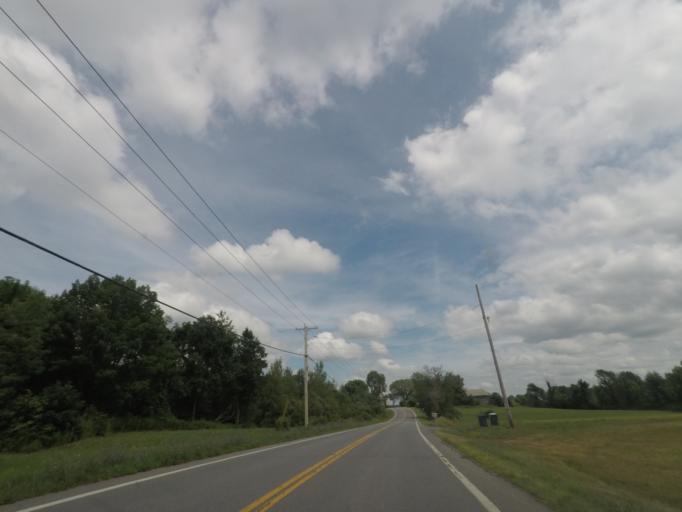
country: US
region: New York
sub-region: Saratoga County
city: Stillwater
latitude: 43.0241
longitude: -73.6739
